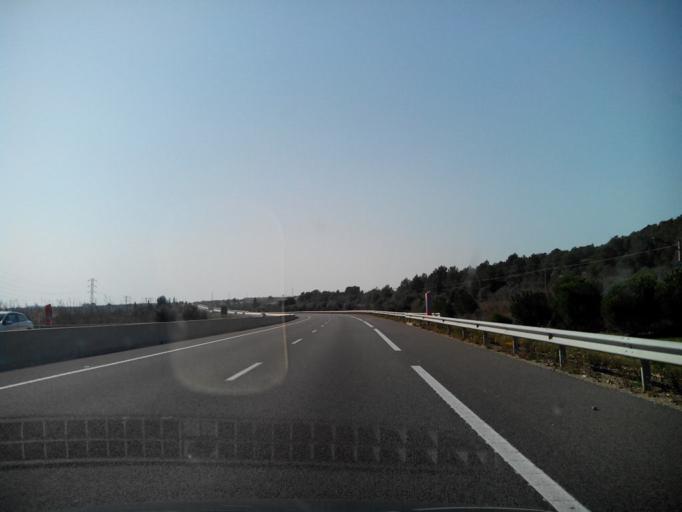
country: ES
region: Catalonia
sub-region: Provincia de Tarragona
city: Alcover
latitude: 41.2452
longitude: 1.1700
